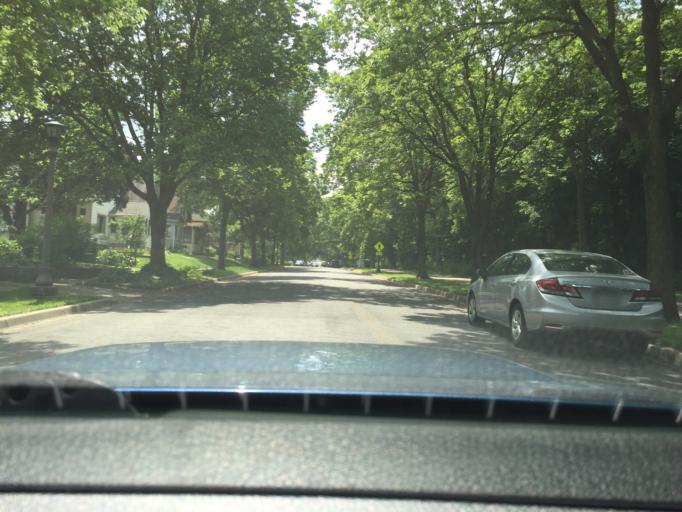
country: US
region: Minnesota
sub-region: Dakota County
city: West Saint Paul
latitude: 44.9286
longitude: -93.1047
